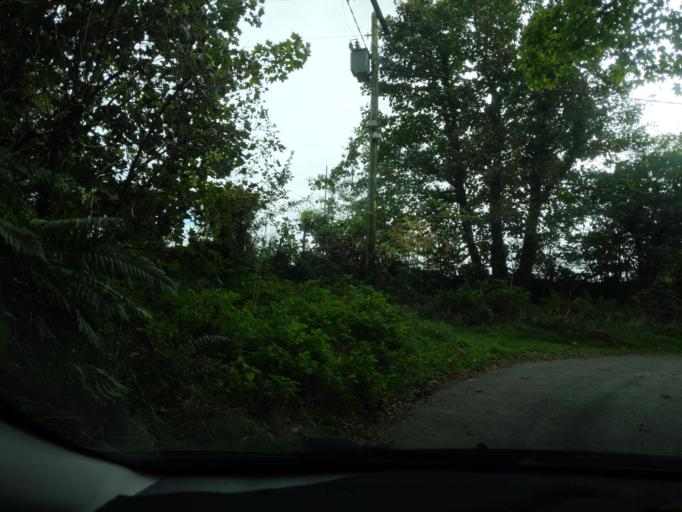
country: GB
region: England
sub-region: Cornwall
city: Lostwithiel
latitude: 50.3944
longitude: -4.7035
